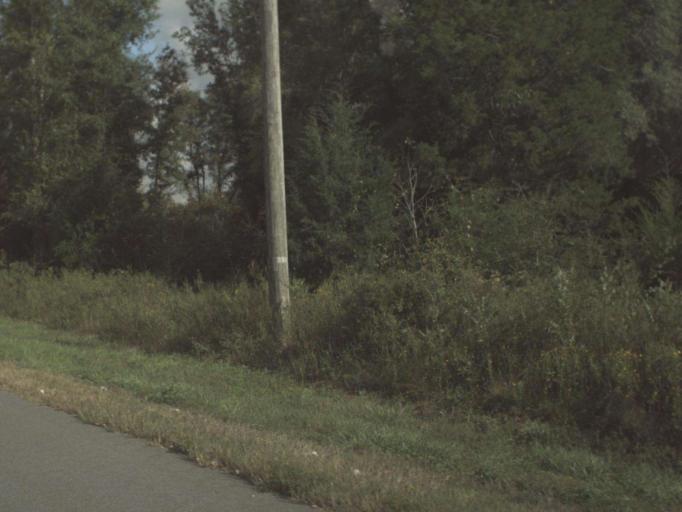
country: US
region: Florida
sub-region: Jackson County
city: Marianna
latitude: 30.6595
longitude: -85.1635
